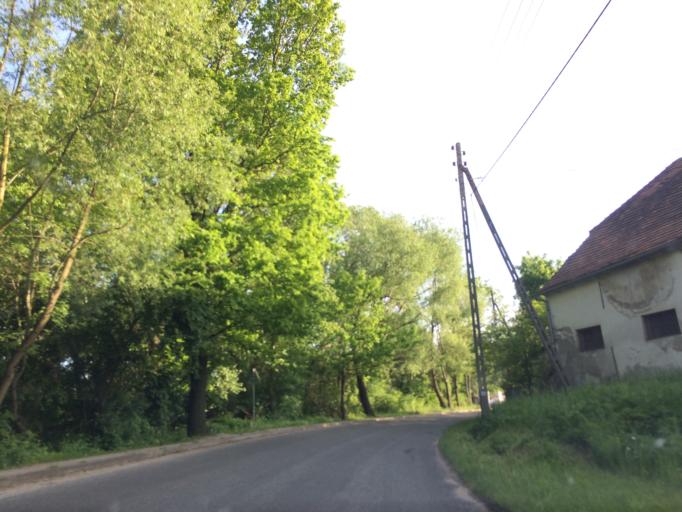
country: PL
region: Lower Silesian Voivodeship
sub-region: Powiat swidnicki
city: Swidnica
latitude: 50.7772
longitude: 16.5029
